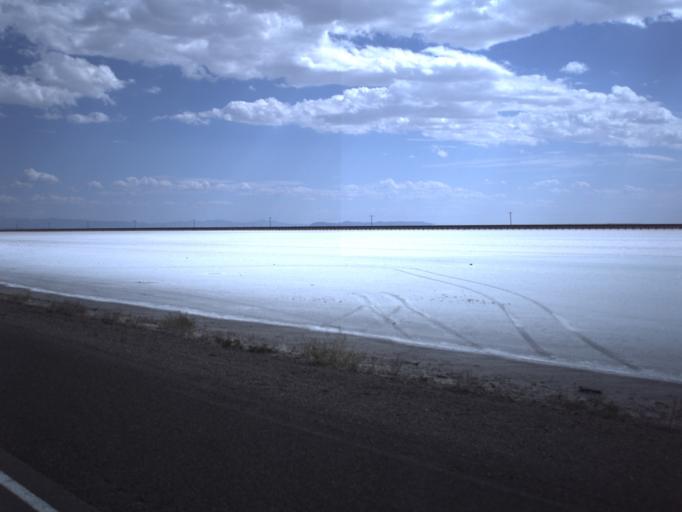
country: US
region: Utah
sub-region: Tooele County
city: Wendover
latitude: 40.7355
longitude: -113.7062
